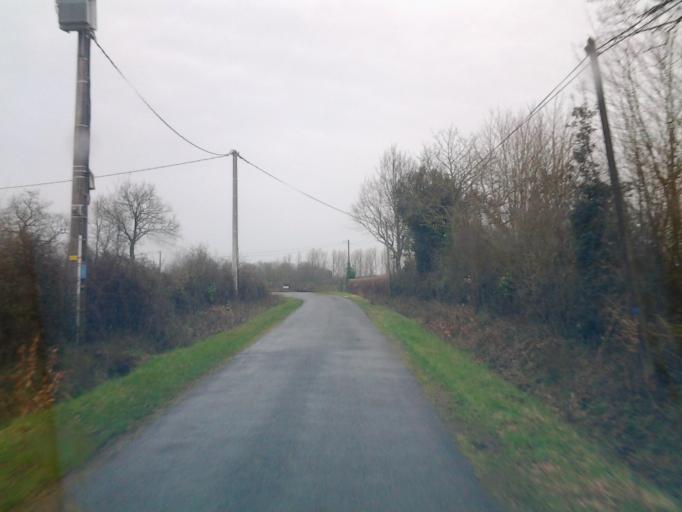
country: FR
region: Pays de la Loire
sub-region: Departement de la Vendee
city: Nesmy
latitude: 46.6355
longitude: -1.3699
